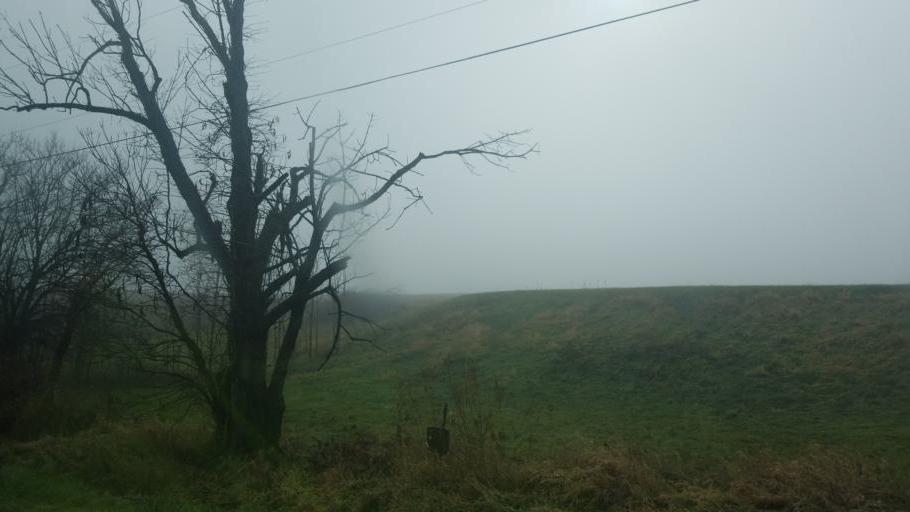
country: US
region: Ohio
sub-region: Champaign County
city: North Lewisburg
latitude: 40.3092
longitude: -83.6183
